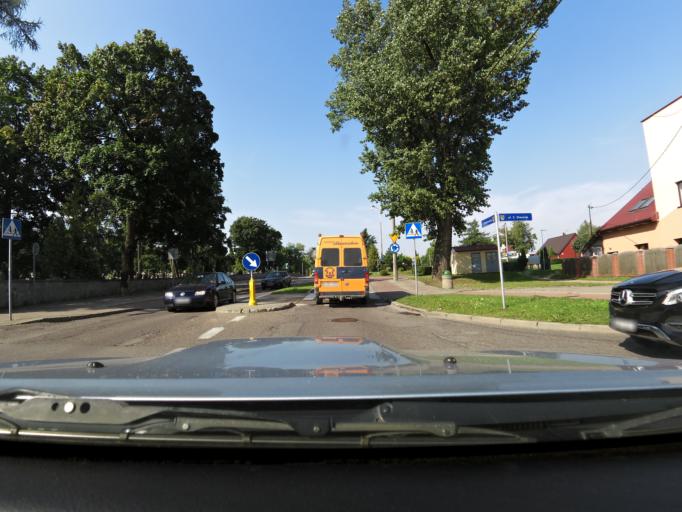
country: PL
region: Podlasie
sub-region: Suwalki
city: Suwalki
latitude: 54.0992
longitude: 22.9185
